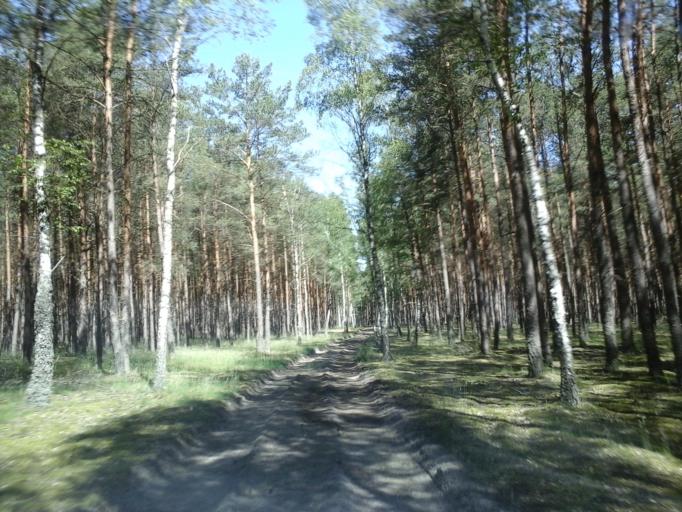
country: PL
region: West Pomeranian Voivodeship
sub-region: Powiat drawski
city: Kalisz Pomorski
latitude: 53.1811
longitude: 15.9839
